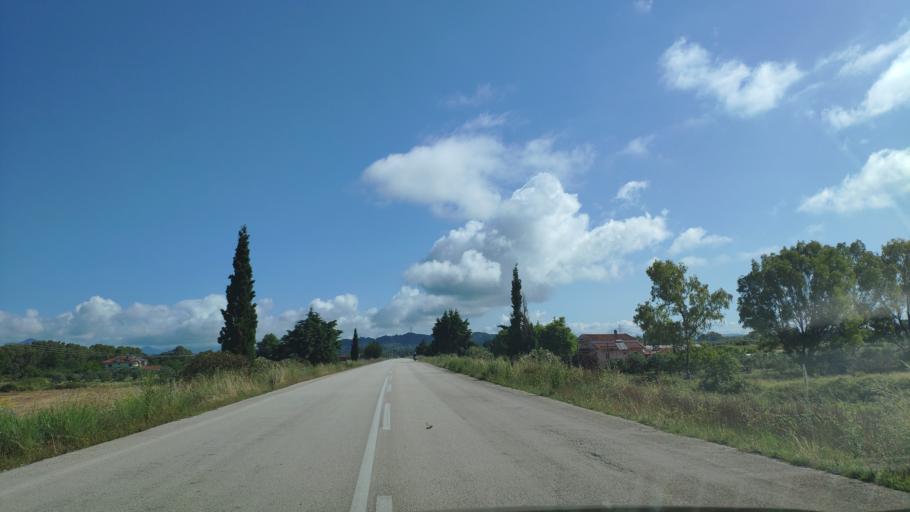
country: GR
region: Epirus
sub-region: Nomos Prevezis
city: Preveza
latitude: 38.9971
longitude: 20.7150
